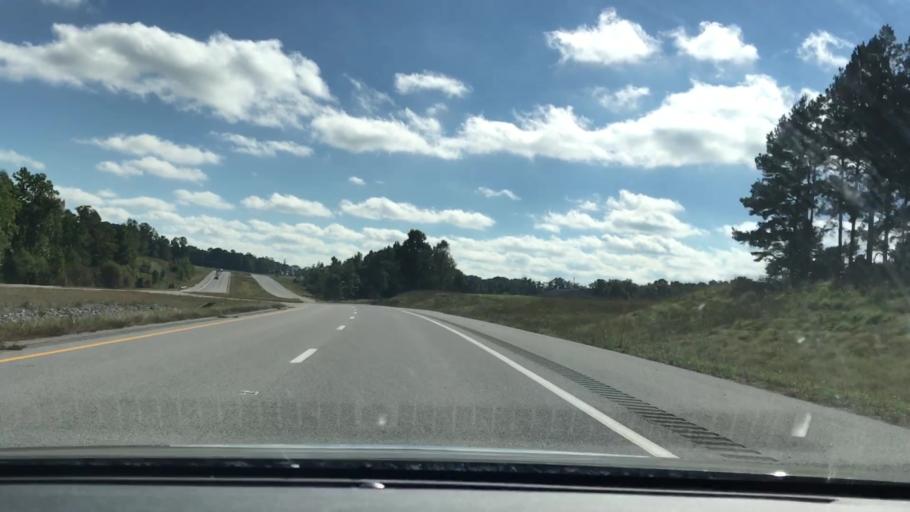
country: US
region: Tennessee
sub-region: Fentress County
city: Grimsley
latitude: 36.3284
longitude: -84.9624
